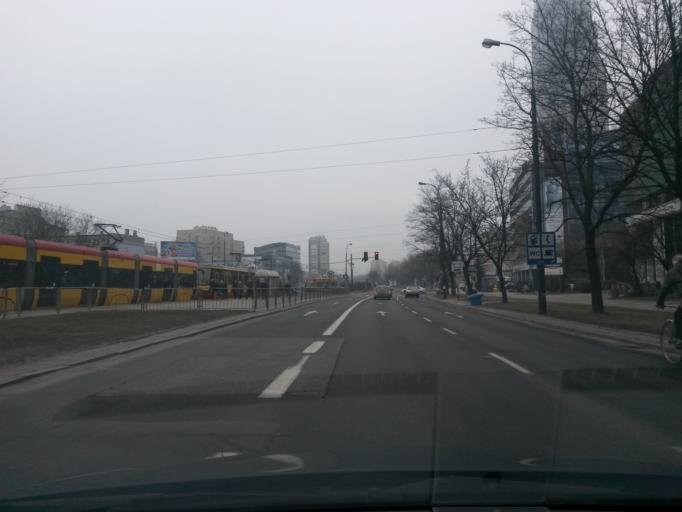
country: PL
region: Masovian Voivodeship
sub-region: Warszawa
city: Wola
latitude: 52.2325
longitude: 20.9829
